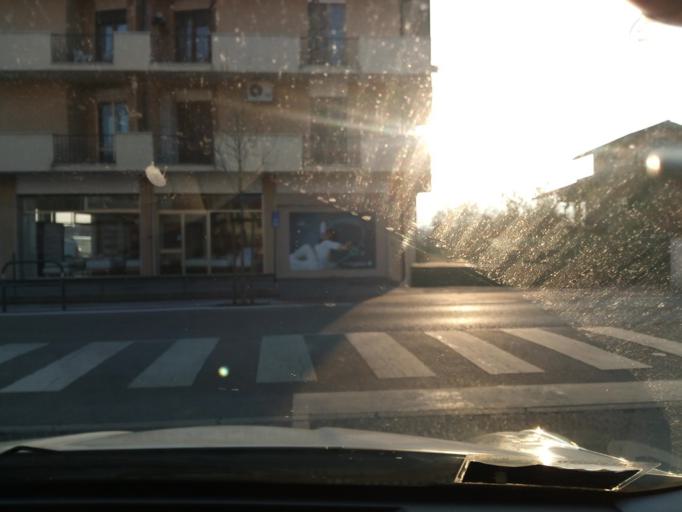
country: IT
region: Veneto
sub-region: Provincia di Vicenza
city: Schio
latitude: 45.7119
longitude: 11.3731
